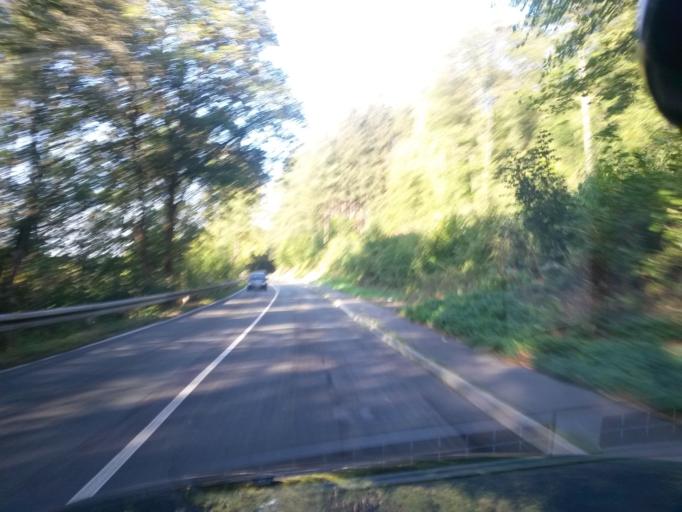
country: DE
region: North Rhine-Westphalia
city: Bergneustadt
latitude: 51.0319
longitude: 7.6286
